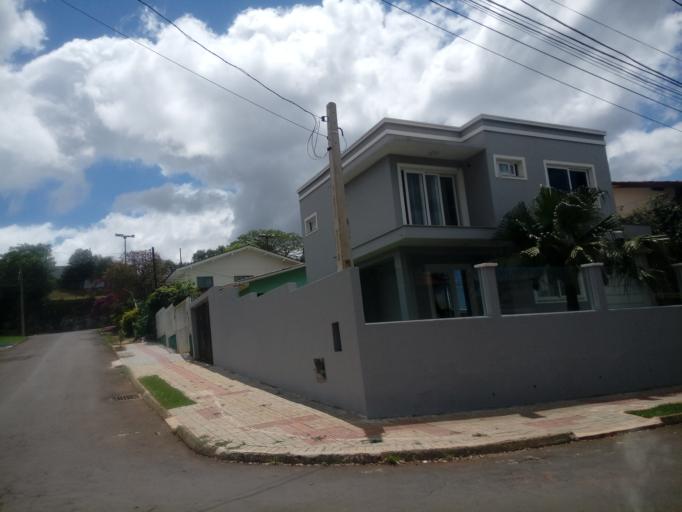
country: BR
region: Santa Catarina
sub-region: Chapeco
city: Chapeco
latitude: -27.0980
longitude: -52.6393
